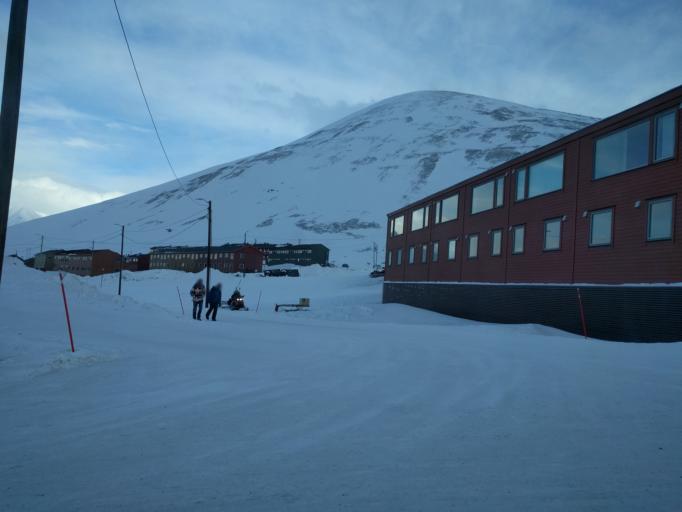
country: SJ
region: Svalbard
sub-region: Spitsbergen
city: Longyearbyen
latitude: 78.2135
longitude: 15.6206
